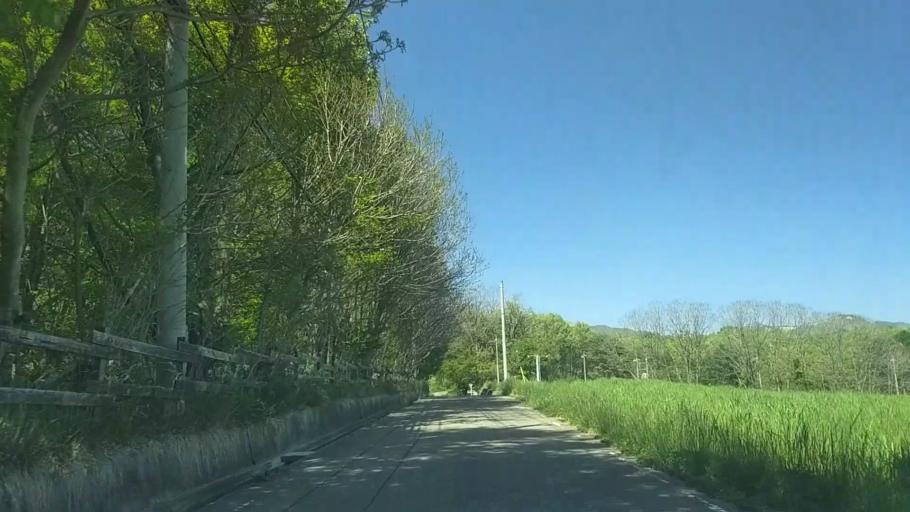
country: JP
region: Yamanashi
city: Nirasaki
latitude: 35.8935
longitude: 138.4384
